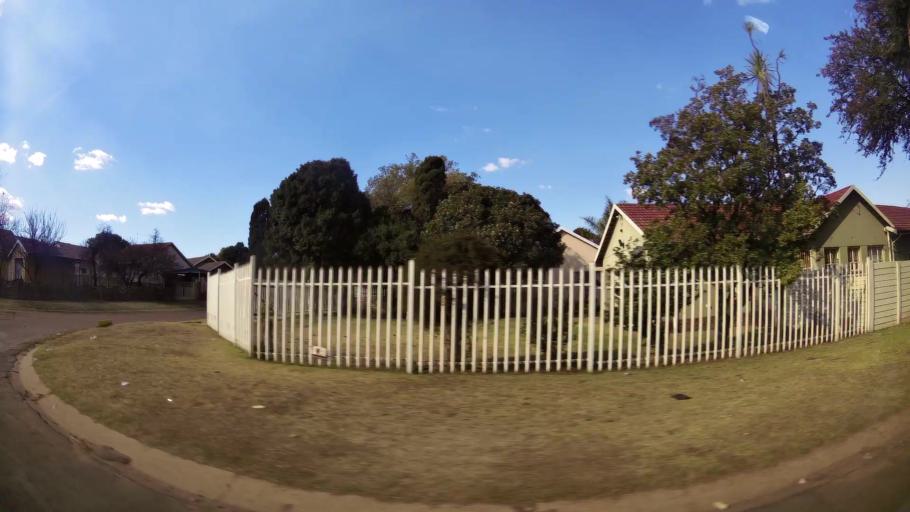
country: ZA
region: Mpumalanga
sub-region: Nkangala District Municipality
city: Witbank
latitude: -25.9074
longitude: 29.2262
